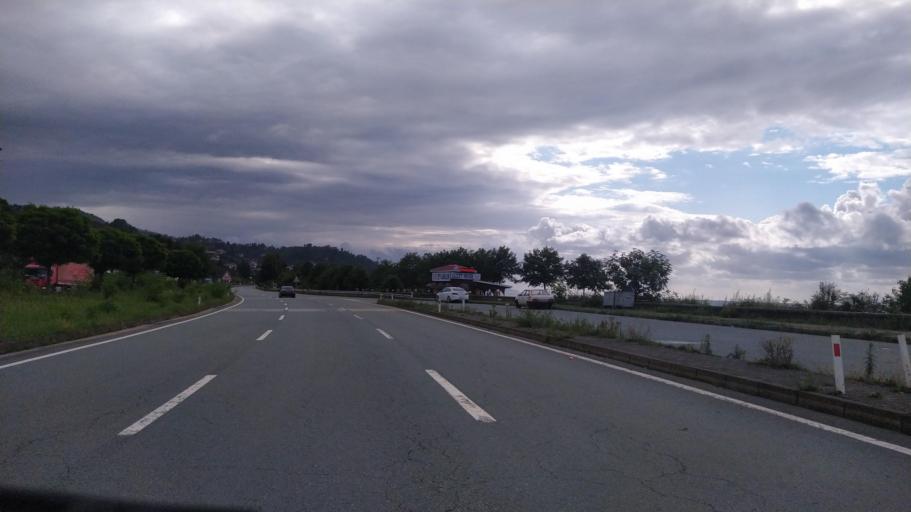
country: TR
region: Rize
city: Ardesen
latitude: 41.2164
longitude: 41.0587
